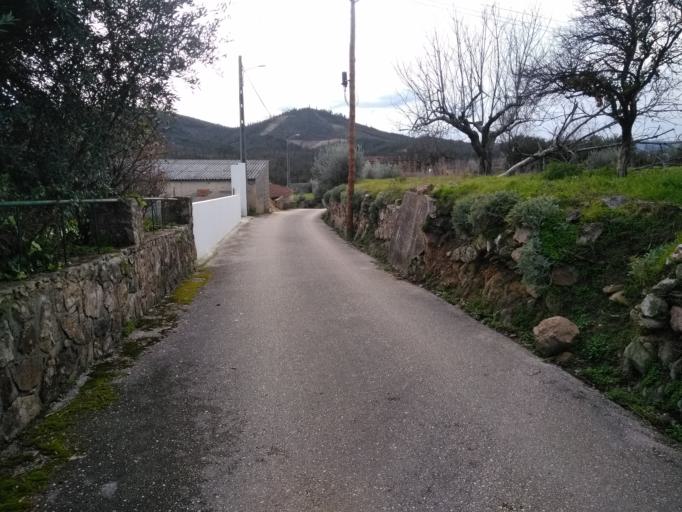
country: PT
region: Coimbra
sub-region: Vila Nova de Poiares
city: Poiares
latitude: 40.1941
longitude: -8.2107
